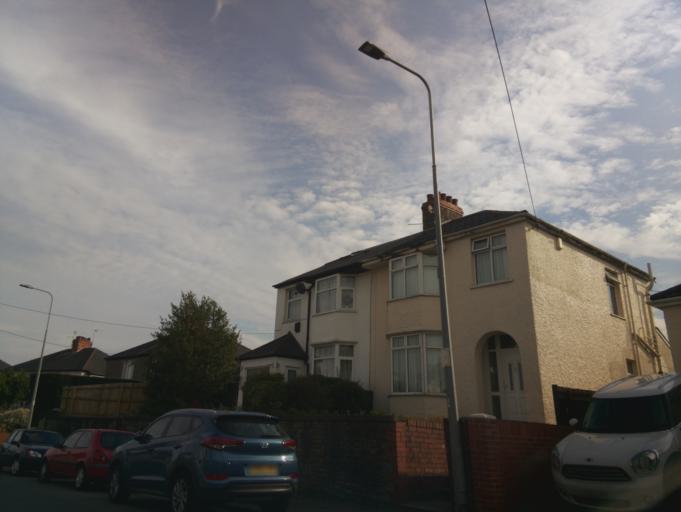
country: GB
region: Wales
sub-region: Cardiff
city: Cardiff
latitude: 51.5060
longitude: -3.1300
